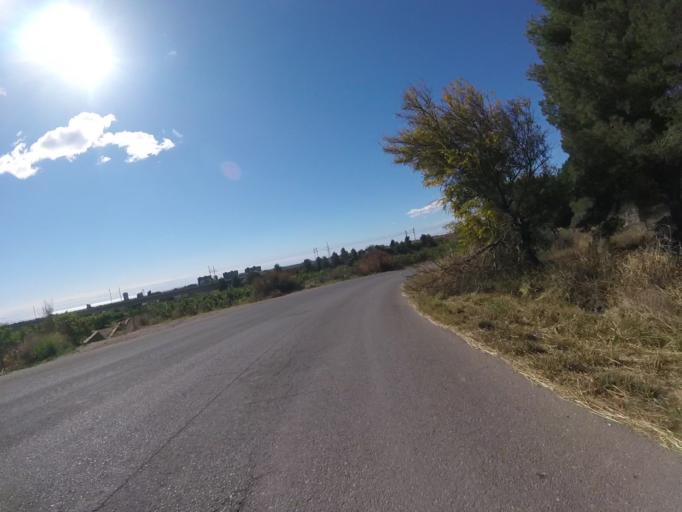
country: ES
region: Valencia
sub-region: Provincia de Castello
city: Benicassim
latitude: 40.0643
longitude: 0.0718
